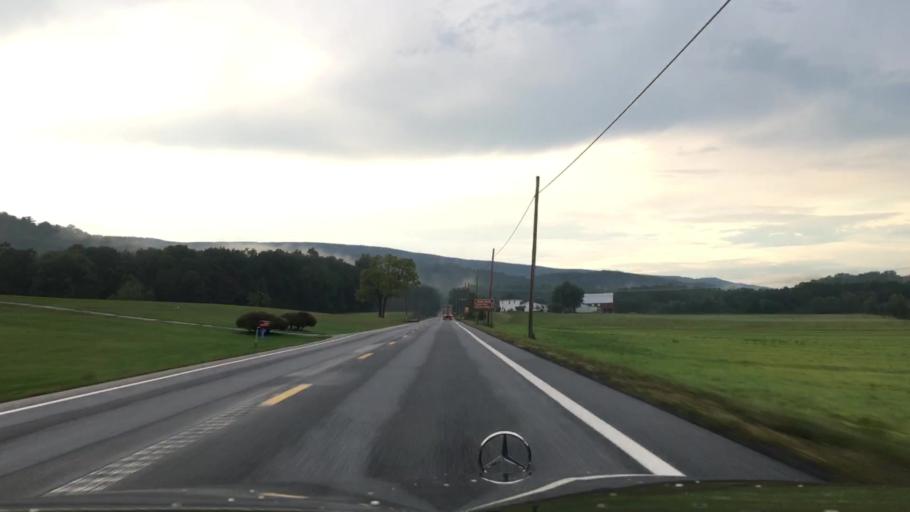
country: US
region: West Virginia
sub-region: Morgan County
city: Berkeley Springs
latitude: 39.4515
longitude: -78.3096
